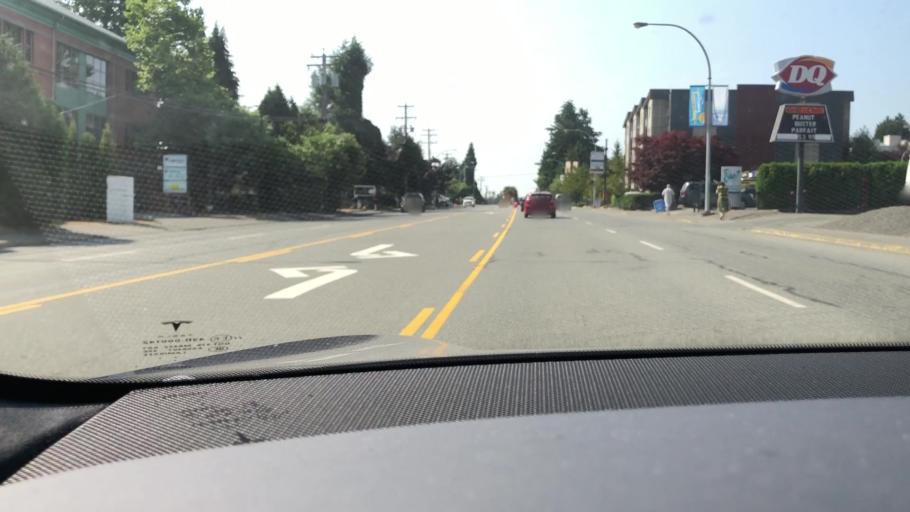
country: US
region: Washington
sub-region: Whatcom County
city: Point Roberts
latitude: 49.0312
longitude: -123.0687
